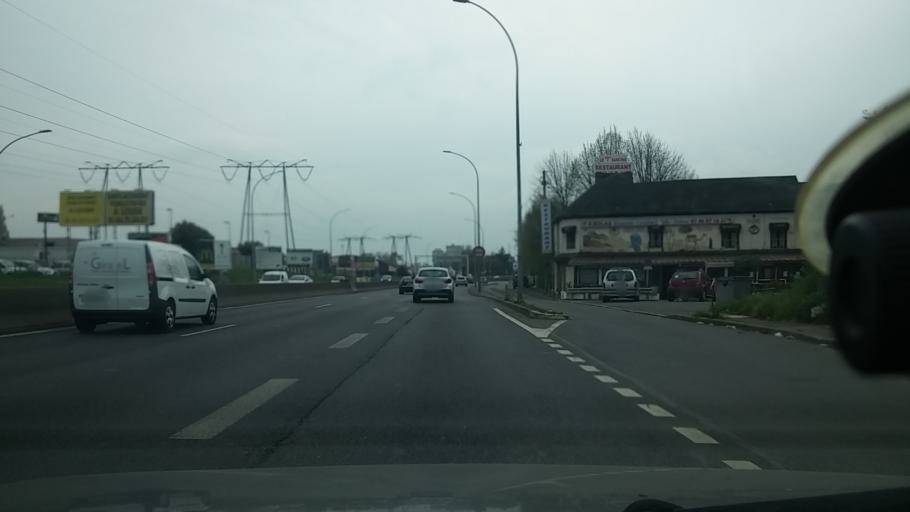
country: FR
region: Ile-de-France
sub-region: Departement du Val-de-Marne
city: Rungis
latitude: 48.7518
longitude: 2.3689
